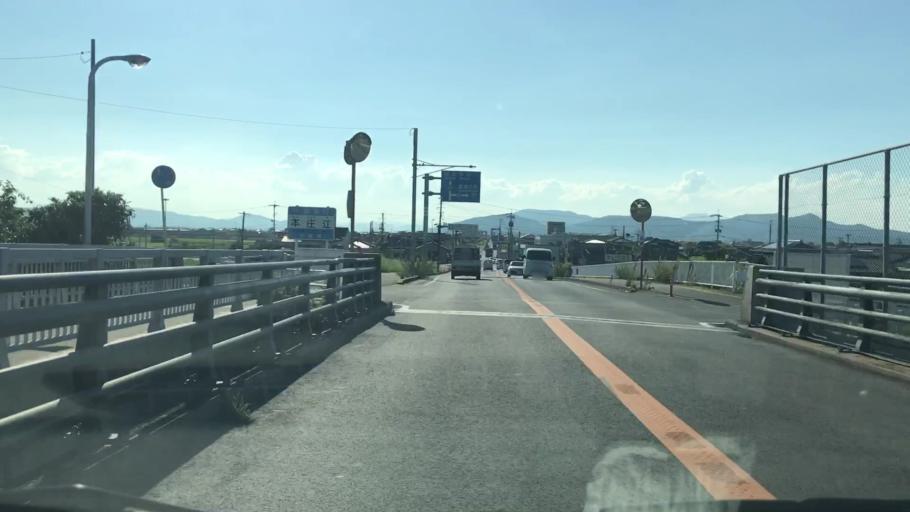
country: JP
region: Saga Prefecture
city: Saga-shi
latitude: 33.2191
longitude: 130.2596
